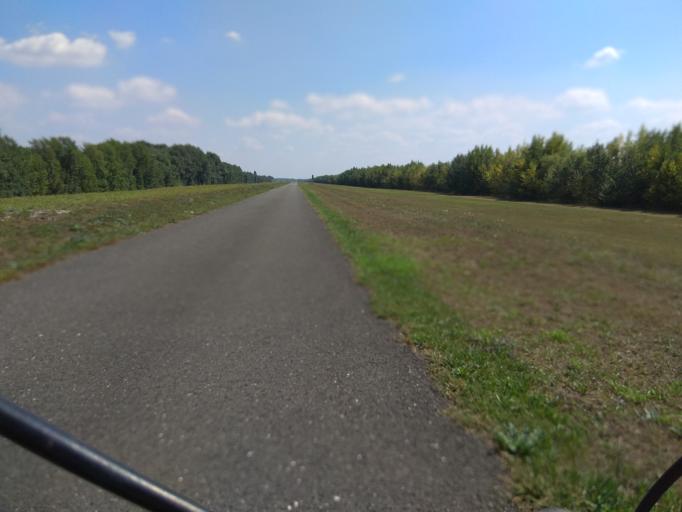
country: SK
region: Trnavsky
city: Gabcikovo
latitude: 47.8524
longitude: 17.5747
